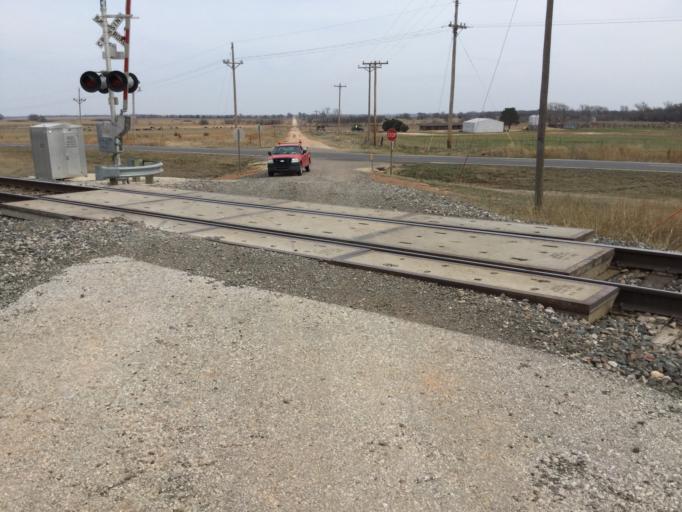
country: US
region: Kansas
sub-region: Barber County
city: Kiowa
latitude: 37.1380
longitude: -98.3527
